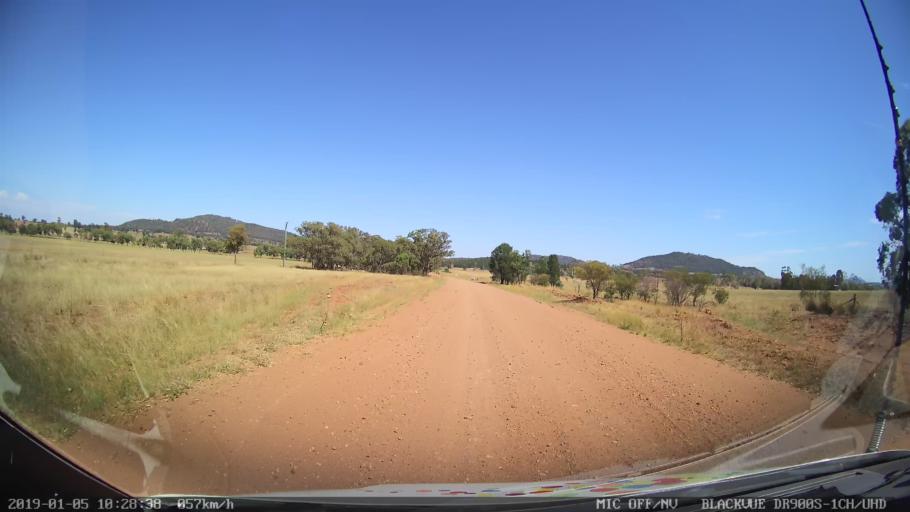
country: AU
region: New South Wales
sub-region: Gilgandra
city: Gilgandra
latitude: -31.5439
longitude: 148.9370
